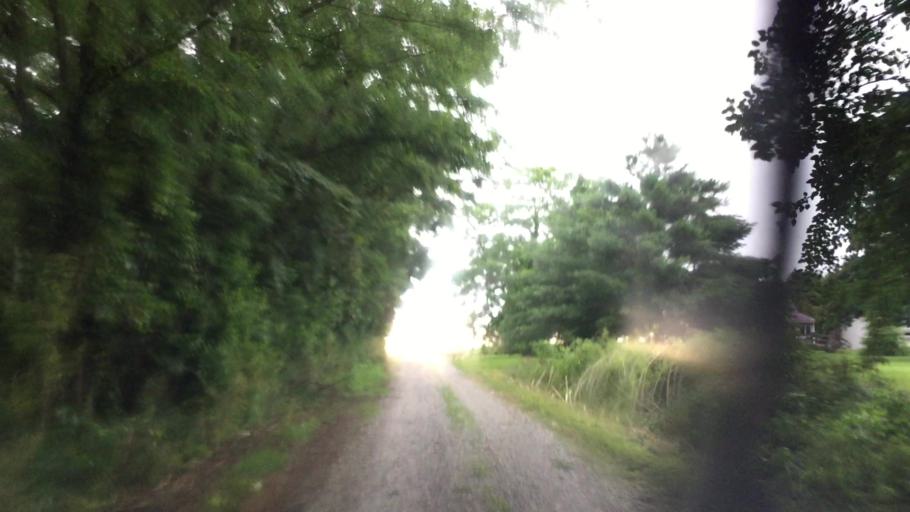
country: US
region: Illinois
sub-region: Hancock County
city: Nauvoo
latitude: 40.5505
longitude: -91.3513
